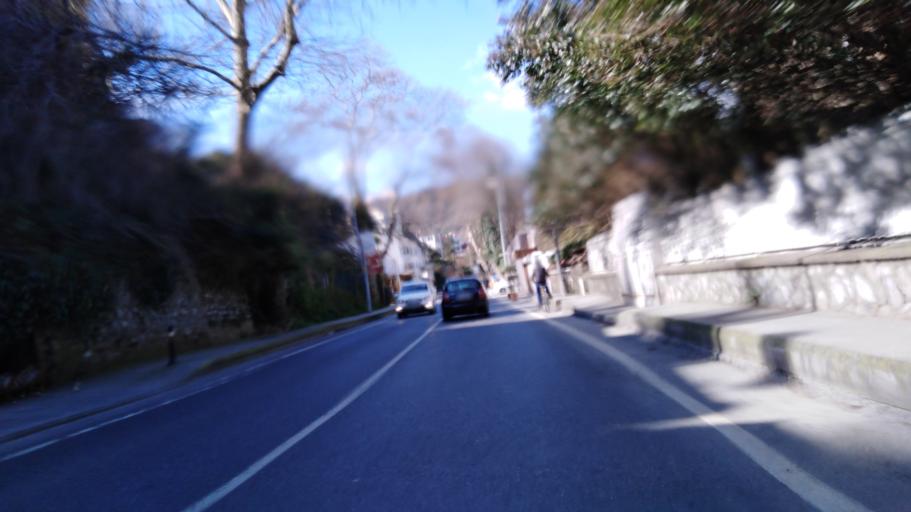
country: TR
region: Istanbul
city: Arikoey
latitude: 41.1477
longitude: 29.0501
